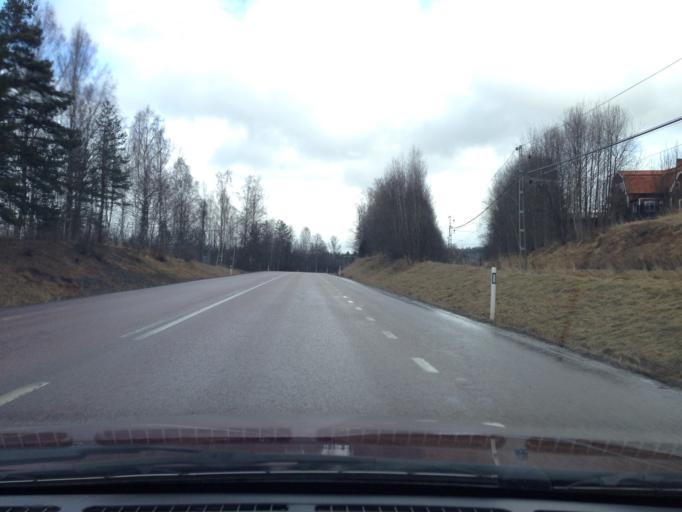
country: SE
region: Dalarna
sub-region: Ludvika Kommun
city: Ludvika
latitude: 60.1521
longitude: 15.2265
